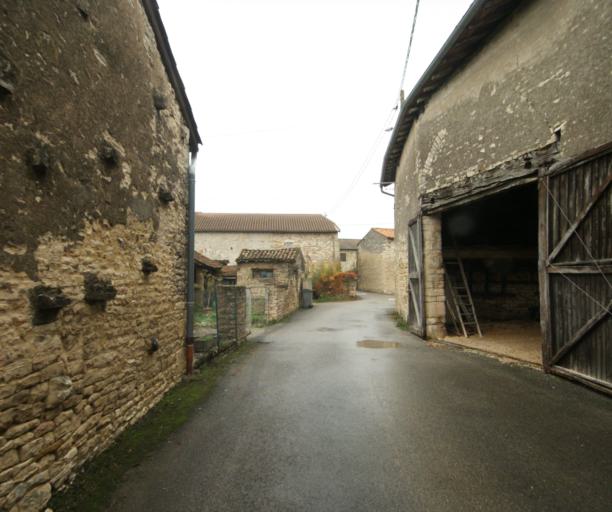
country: FR
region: Bourgogne
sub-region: Departement de Saone-et-Loire
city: Saint-Martin-Belle-Roche
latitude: 46.4700
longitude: 4.8515
